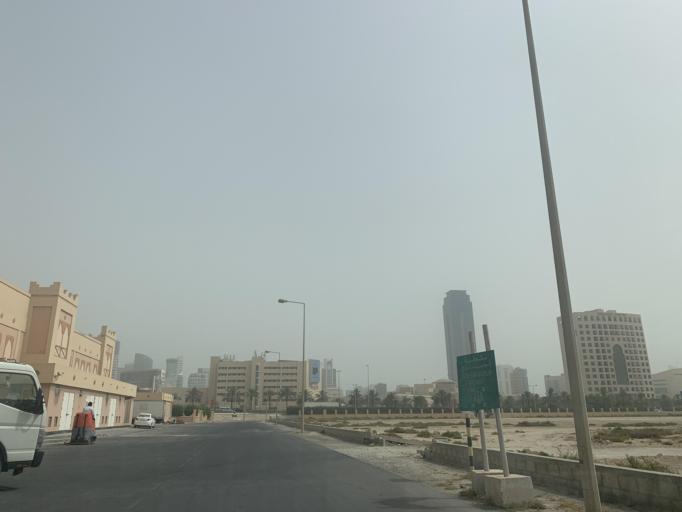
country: BH
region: Manama
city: Jidd Hafs
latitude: 26.2293
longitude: 50.5388
